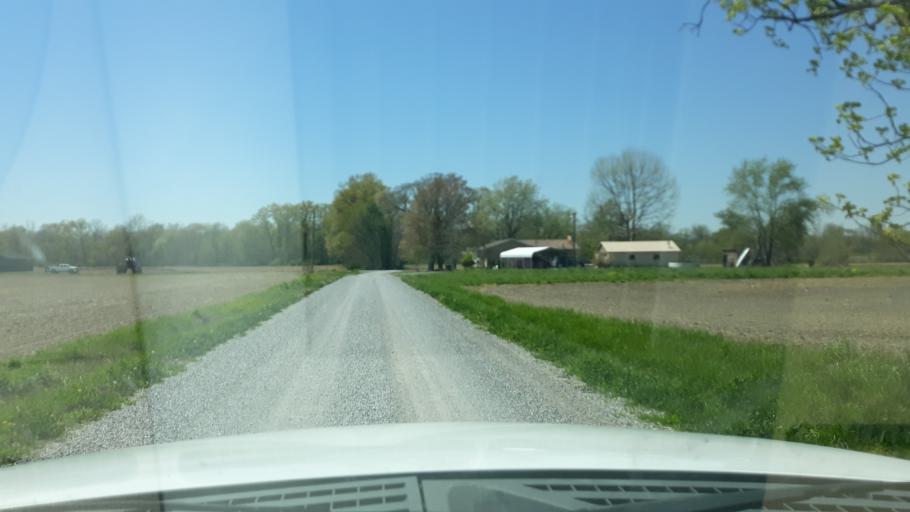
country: US
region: Illinois
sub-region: Saline County
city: Harrisburg
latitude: 37.8923
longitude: -88.6773
